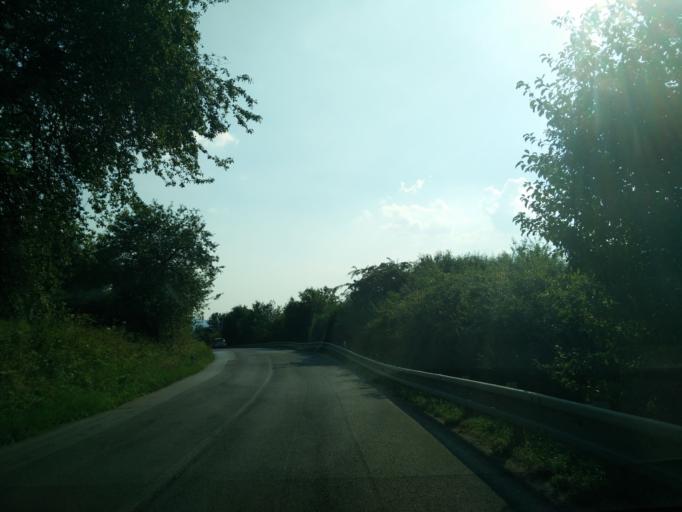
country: SK
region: Zilinsky
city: Rajec
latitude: 49.1145
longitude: 18.6520
